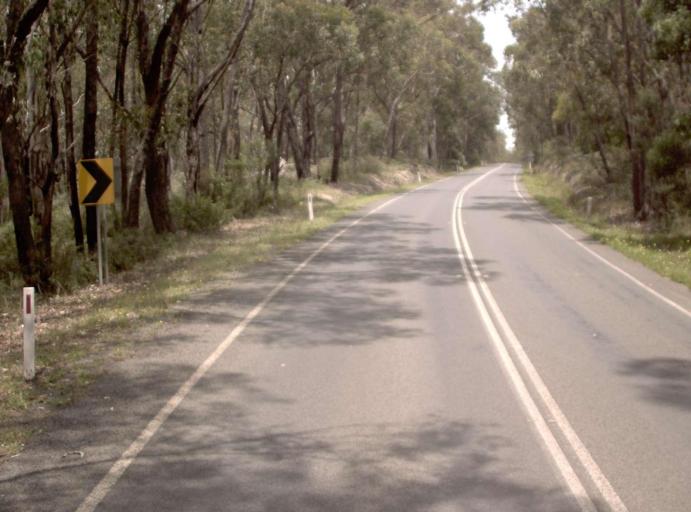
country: AU
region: Victoria
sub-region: Latrobe
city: Traralgon
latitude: -38.4087
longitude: 146.7521
